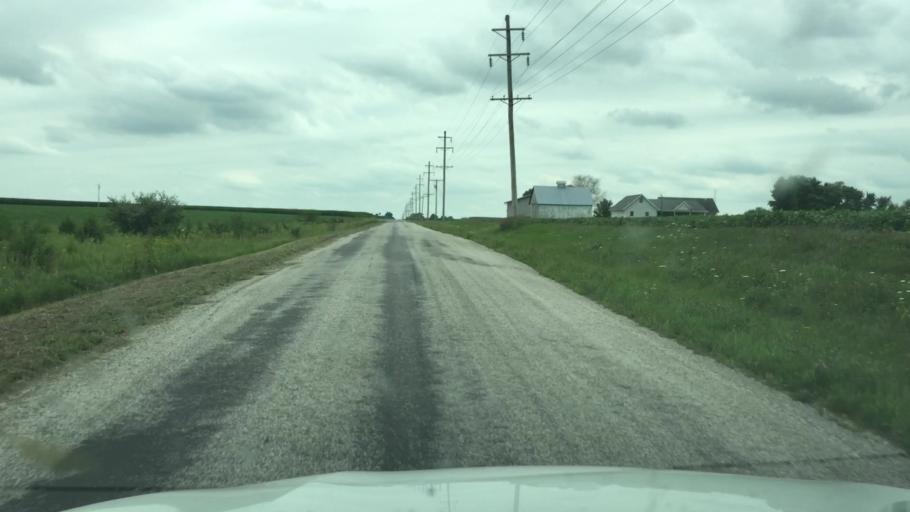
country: US
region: Illinois
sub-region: Hancock County
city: Carthage
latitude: 40.3445
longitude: -91.0823
